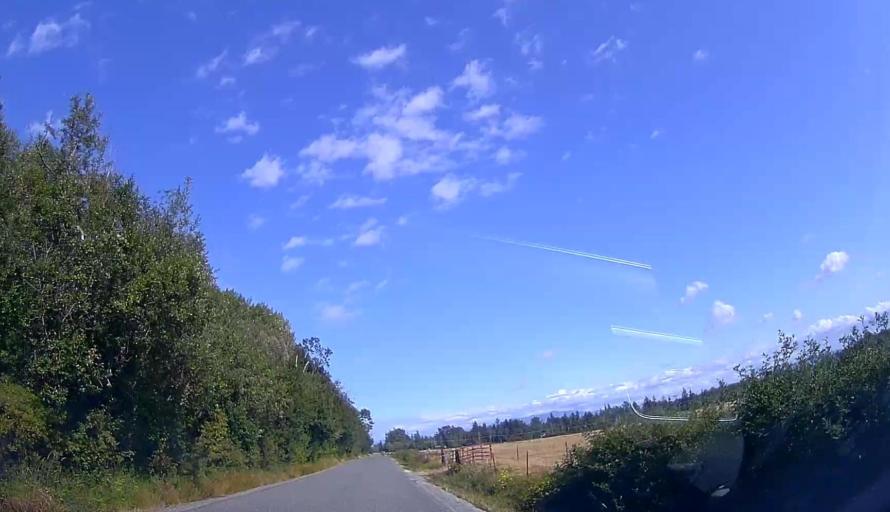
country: US
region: Washington
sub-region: Skagit County
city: Burlington
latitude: 48.4939
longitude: -122.4533
